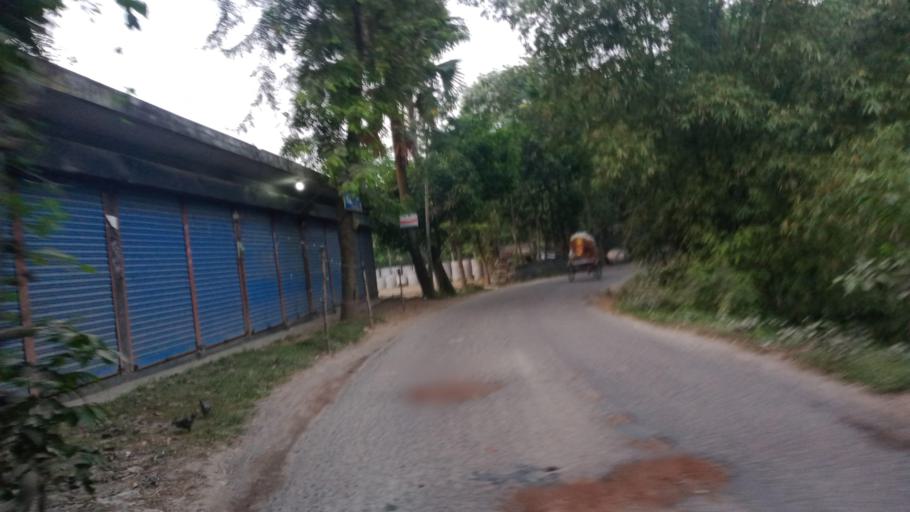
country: BD
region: Chittagong
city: Hajiganj
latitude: 23.3754
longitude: 90.9837
